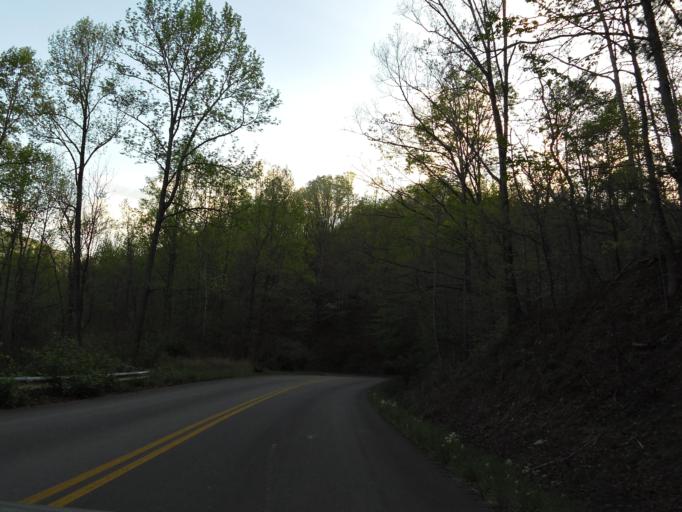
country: US
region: Kentucky
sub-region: Bell County
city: Middlesboro
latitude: 36.6021
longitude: -83.8831
